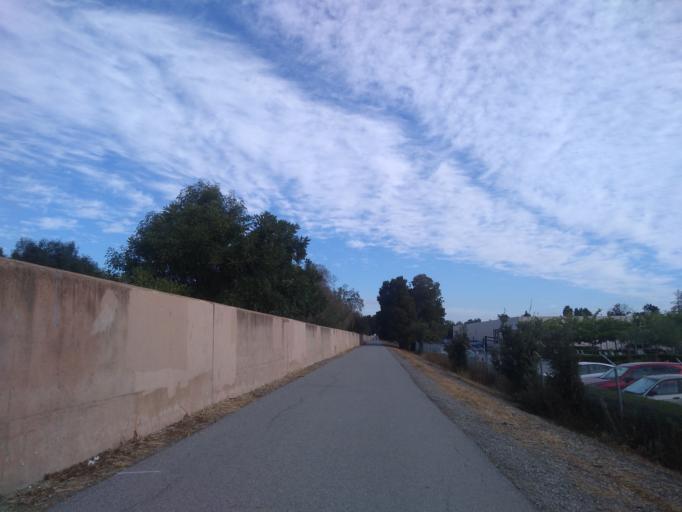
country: US
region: California
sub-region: Santa Clara County
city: Santa Clara
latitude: 37.3990
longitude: -121.9865
